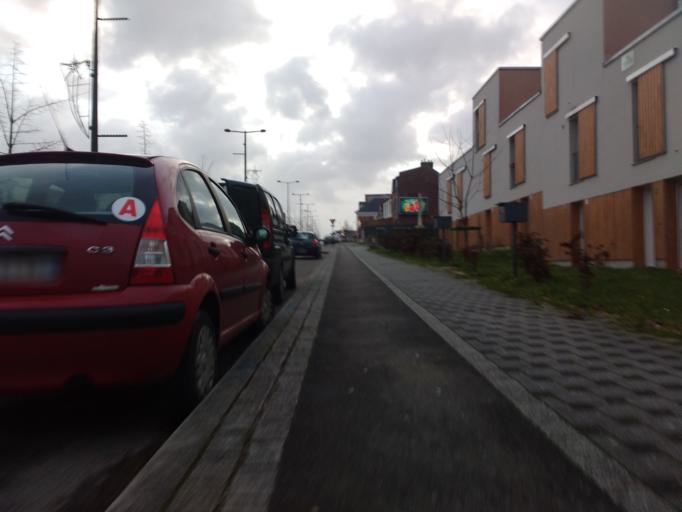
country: FR
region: Picardie
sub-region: Departement de la Somme
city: Longueau
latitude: 49.8699
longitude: 2.3589
